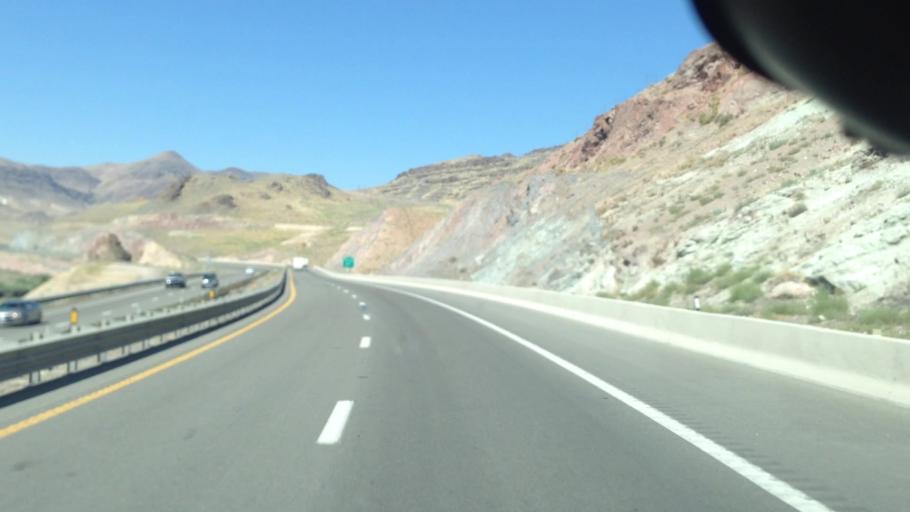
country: US
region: Nevada
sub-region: Lyon County
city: Fernley
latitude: 39.5983
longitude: -119.3585
